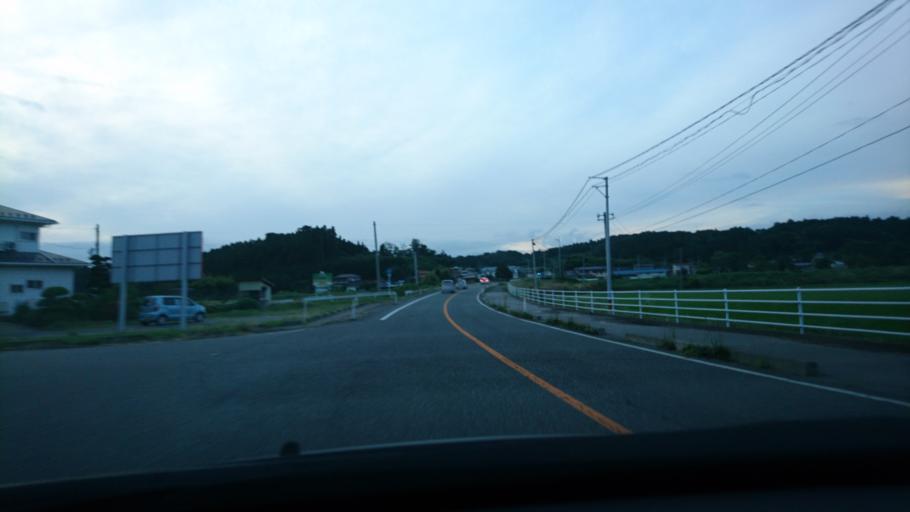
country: JP
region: Iwate
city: Ichinoseki
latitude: 38.7697
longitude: 141.0003
